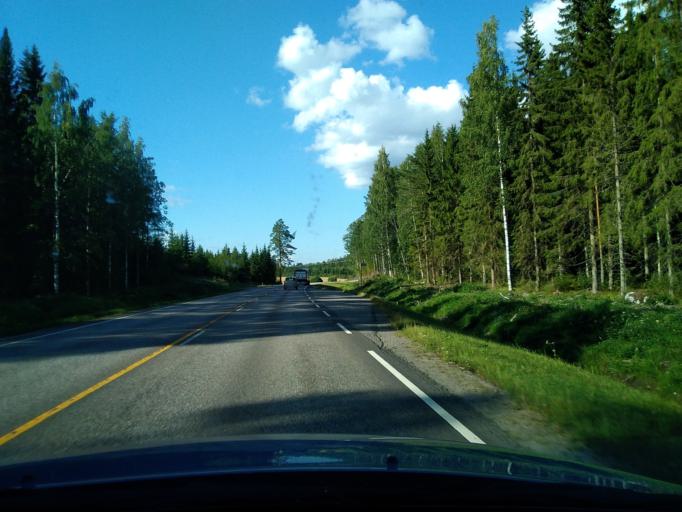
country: FI
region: Central Finland
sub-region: Keuruu
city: Keuruu
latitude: 62.1278
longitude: 24.7363
